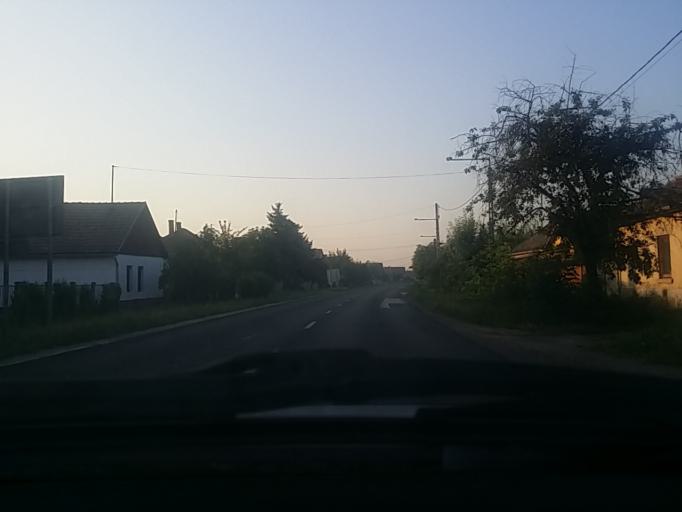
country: HU
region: Pest
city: Szentmartonkata
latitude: 47.4522
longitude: 19.7056
